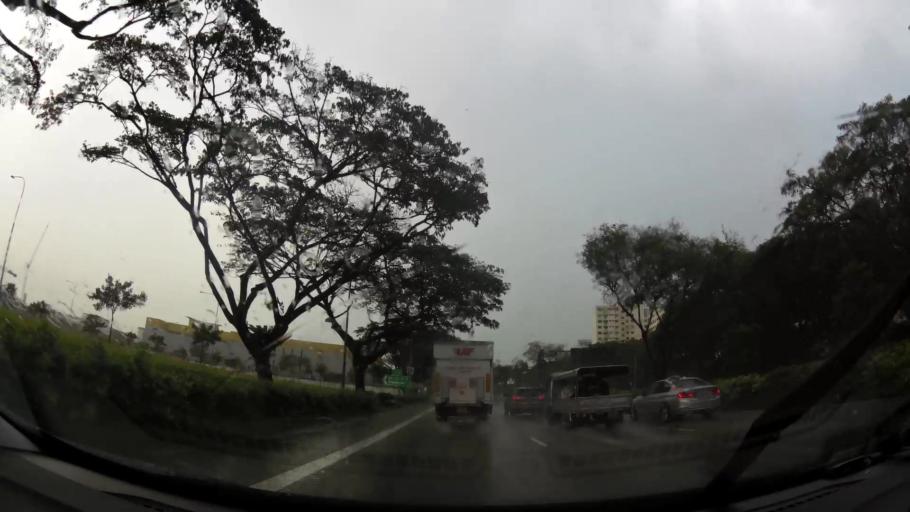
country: MY
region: Johor
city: Kampung Pasir Gudang Baru
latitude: 1.3735
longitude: 103.9363
